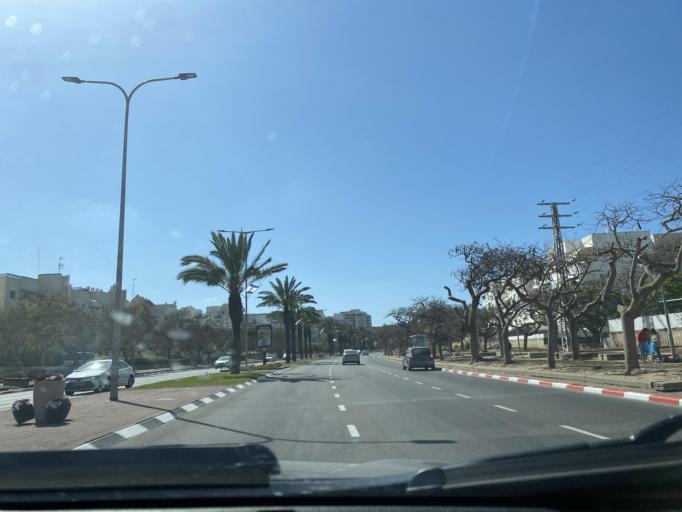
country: IL
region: Southern District
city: Ashqelon
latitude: 31.6739
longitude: 34.5817
